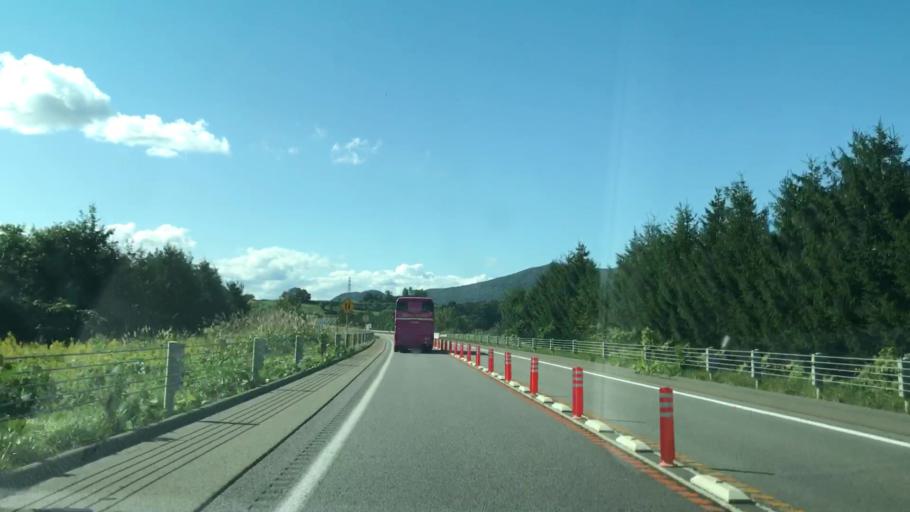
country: JP
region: Hokkaido
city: Date
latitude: 42.4933
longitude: 140.8756
